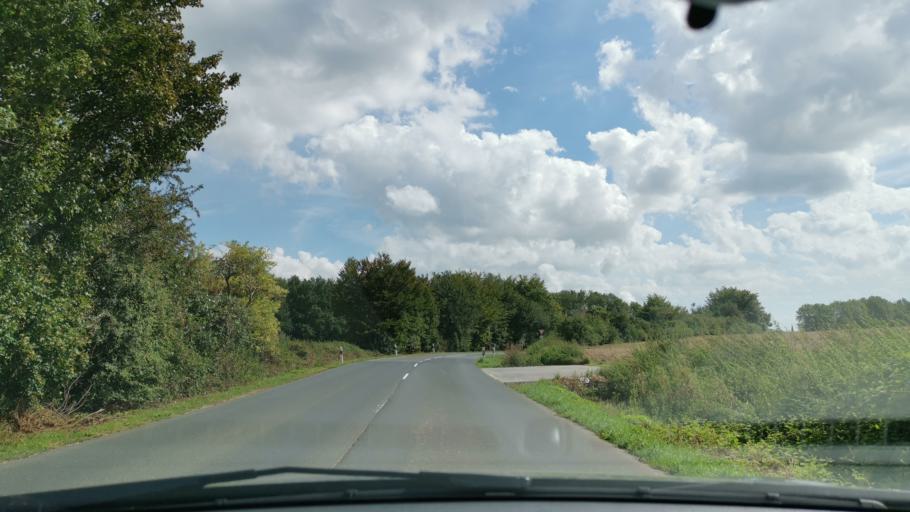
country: DE
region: North Rhine-Westphalia
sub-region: Regierungsbezirk Dusseldorf
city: Grevenbroich
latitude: 51.1028
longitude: 6.5630
